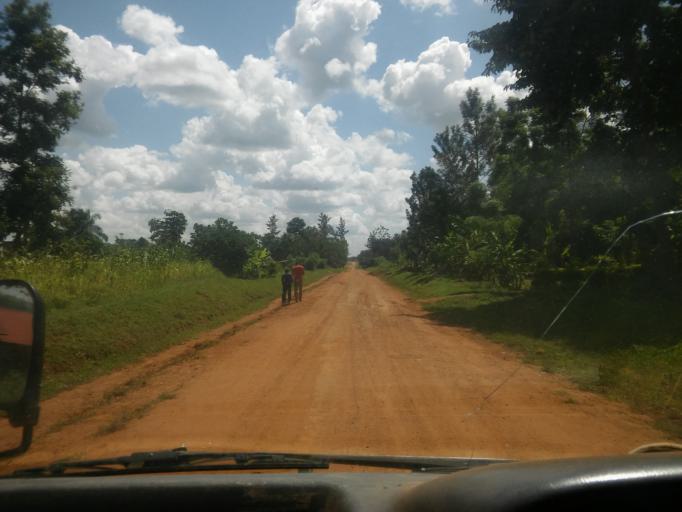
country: UG
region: Eastern Region
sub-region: Kibuku District
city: Kibuku
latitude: 1.1368
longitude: 33.8631
